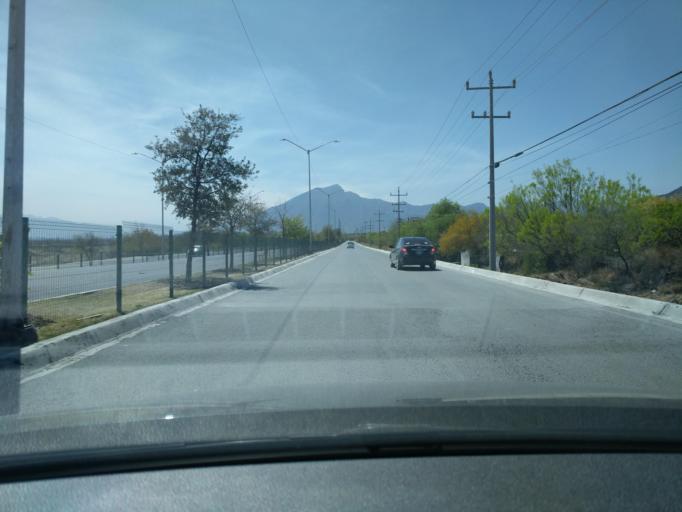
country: MX
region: Nuevo Leon
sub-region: Salinas Victoria
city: Las Torres
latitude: 25.9601
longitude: -100.3022
